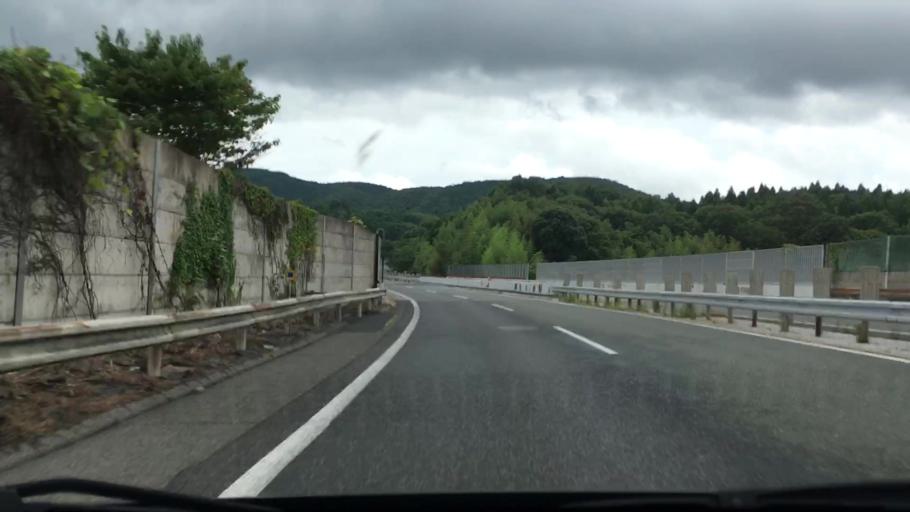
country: JP
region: Okayama
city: Niimi
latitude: 34.9076
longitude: 133.3017
